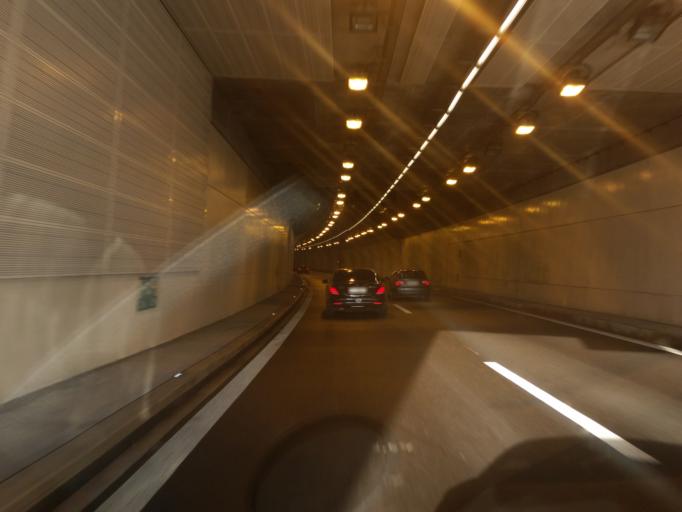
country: CH
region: Zurich
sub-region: Bezirk Affoltern
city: Hedingen
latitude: 47.2962
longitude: 8.4287
